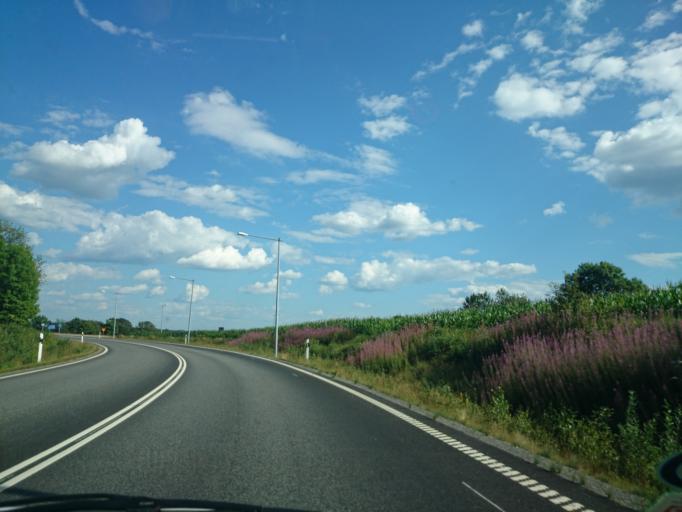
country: SE
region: Joenkoeping
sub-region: Varnamo Kommun
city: Varnamo
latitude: 57.1674
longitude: 14.0312
